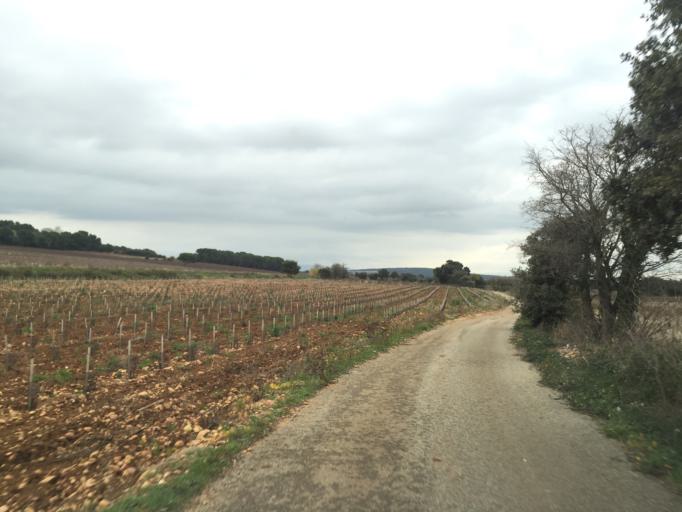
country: FR
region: Provence-Alpes-Cote d'Azur
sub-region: Departement du Vaucluse
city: Chateauneuf-du-Pape
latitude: 44.0424
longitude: 4.8564
